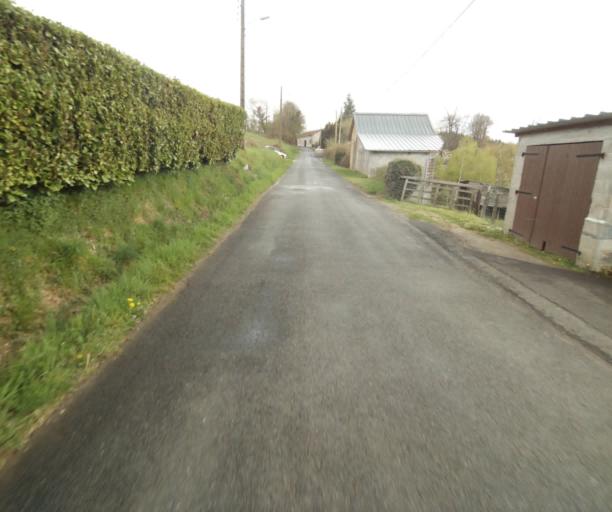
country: FR
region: Limousin
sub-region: Departement de la Correze
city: Tulle
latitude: 45.2761
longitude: 1.7483
